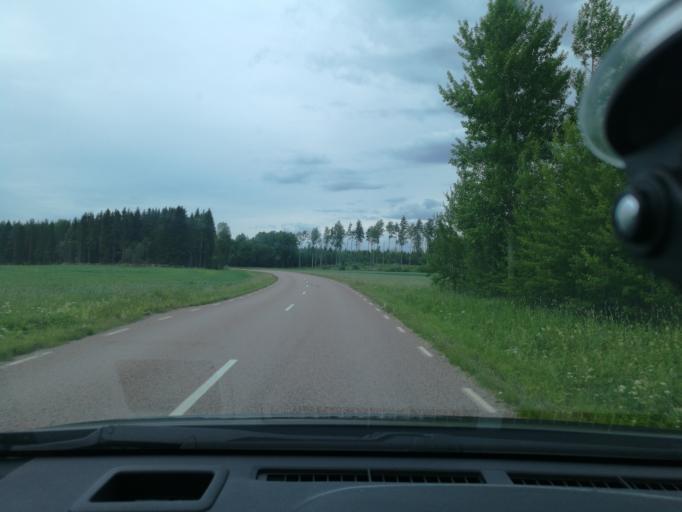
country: SE
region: Vaestmanland
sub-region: Vasteras
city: Skultuna
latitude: 59.7463
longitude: 16.4111
